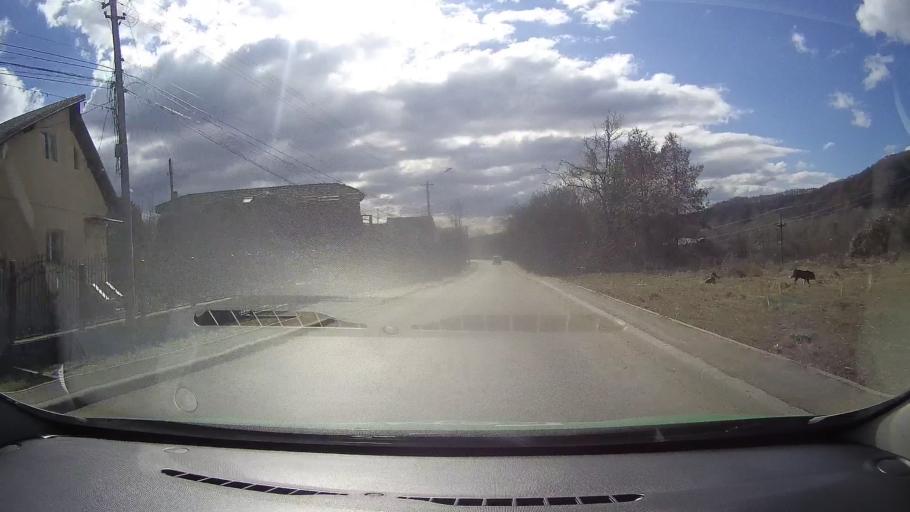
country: RO
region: Dambovita
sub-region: Oras Pucioasa
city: Pucioasa
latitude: 45.0691
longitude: 25.4302
